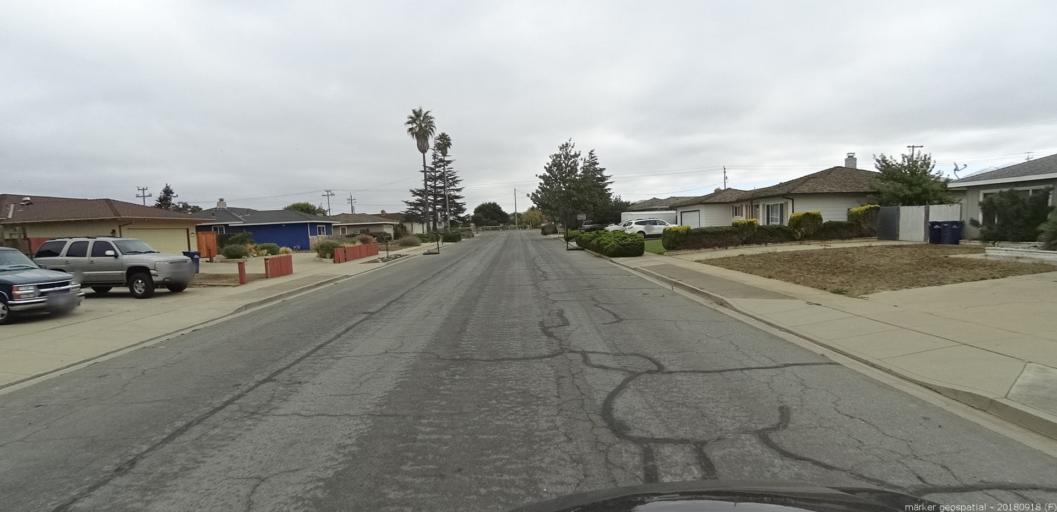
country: US
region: California
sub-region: Monterey County
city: Boronda
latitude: 36.7303
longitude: -121.6313
